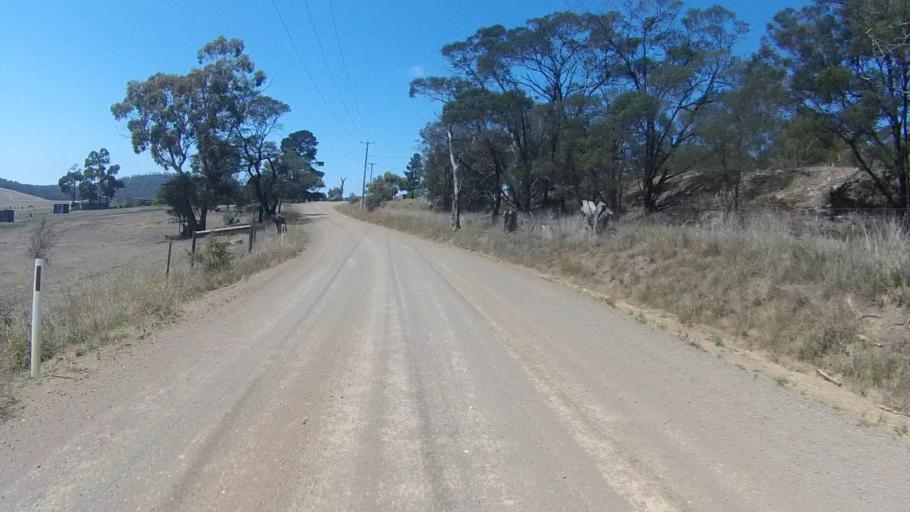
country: AU
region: Tasmania
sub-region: Sorell
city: Sorell
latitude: -42.8227
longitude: 147.6381
